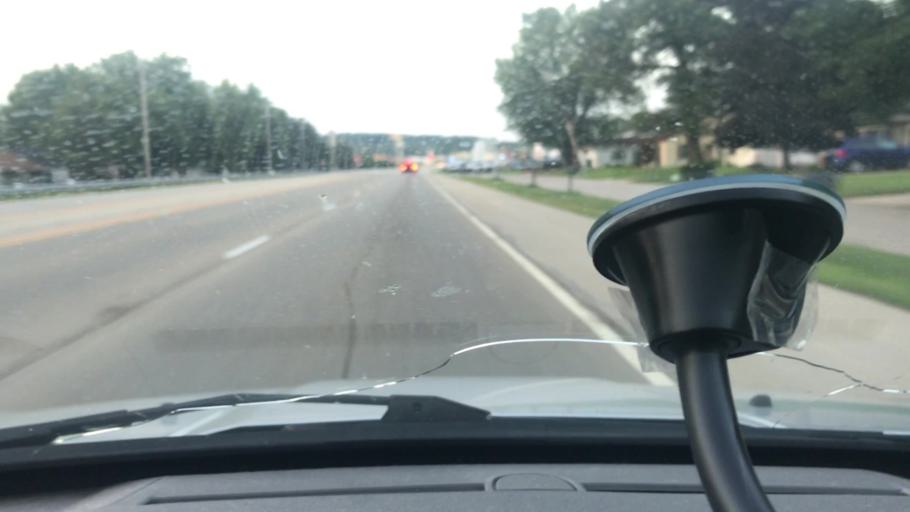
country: US
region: Illinois
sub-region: Tazewell County
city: North Pekin
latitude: 40.6210
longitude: -89.6243
